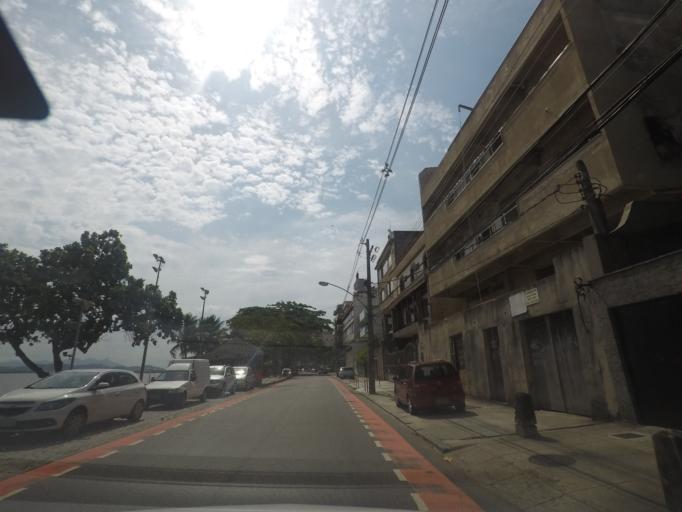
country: BR
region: Rio de Janeiro
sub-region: Rio De Janeiro
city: Rio de Janeiro
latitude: -22.8186
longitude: -43.1951
